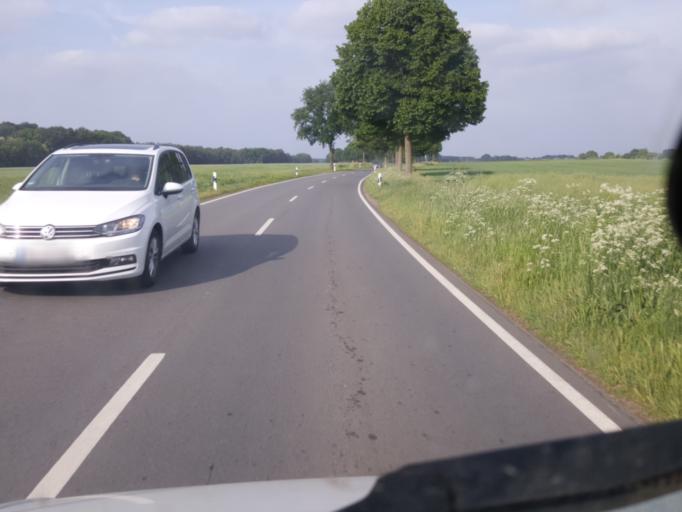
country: DE
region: Lower Saxony
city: Steyerberg
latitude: 52.5717
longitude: 9.0419
